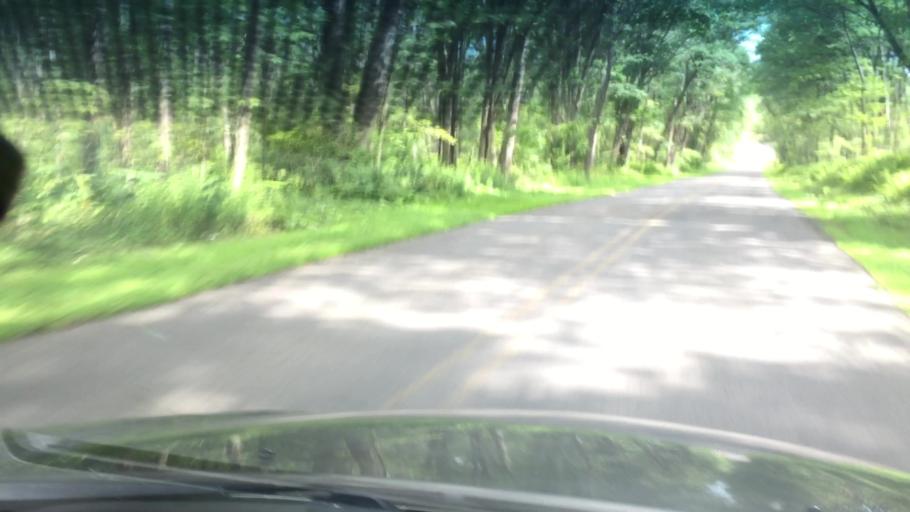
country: US
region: Pennsylvania
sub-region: Luzerne County
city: Harleigh
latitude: 41.0428
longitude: -75.9763
